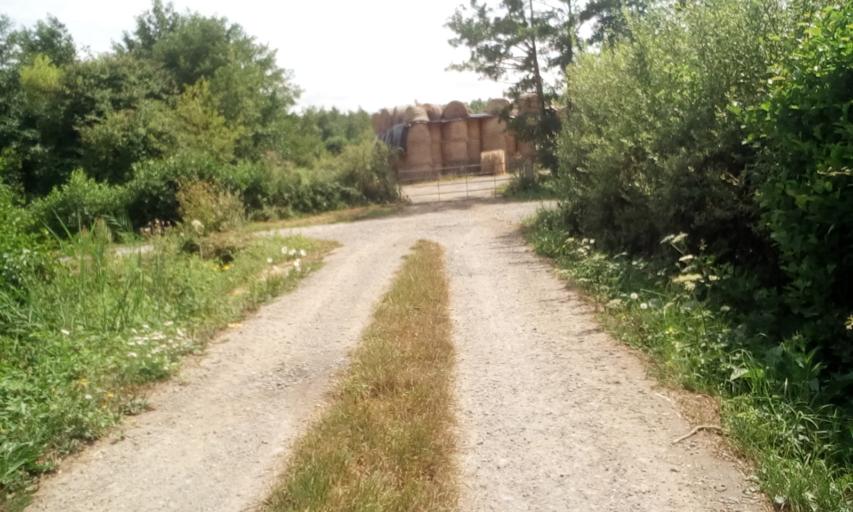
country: FR
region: Lower Normandy
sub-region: Departement du Calvados
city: Bavent
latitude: 49.2400
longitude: -0.1713
